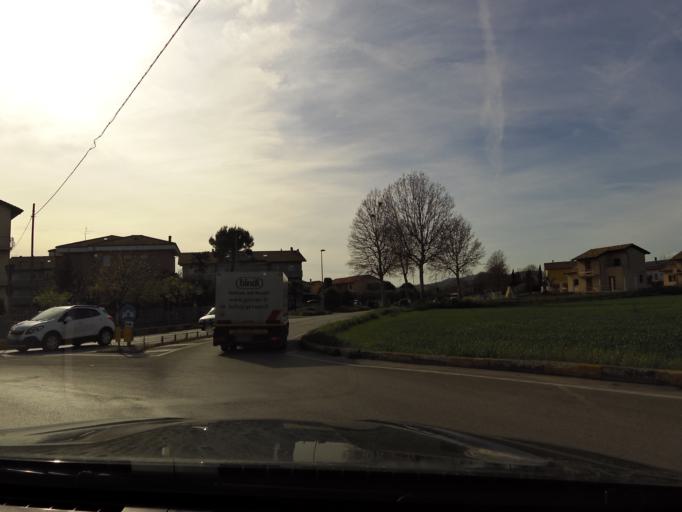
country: IT
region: The Marches
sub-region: Provincia di Ancona
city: Villa Musone
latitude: 43.4475
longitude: 13.6076
